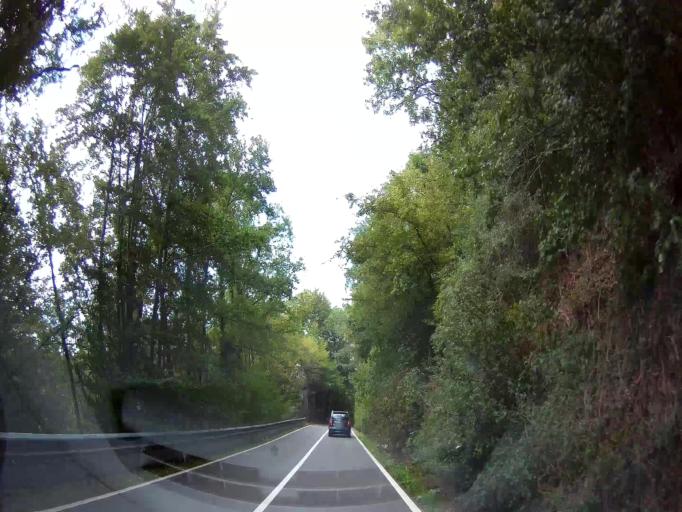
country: BE
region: Wallonia
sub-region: Province de Liege
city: Hamoir
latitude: 50.3901
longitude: 5.5390
